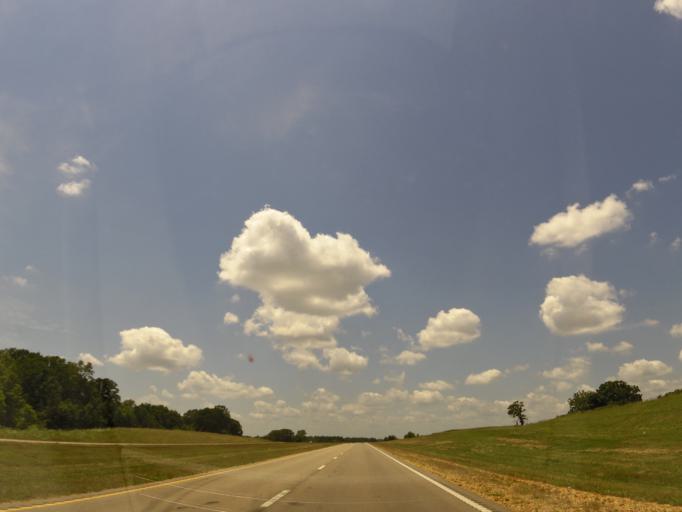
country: US
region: Mississippi
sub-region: Lee County
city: Verona
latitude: 34.2140
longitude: -88.8011
